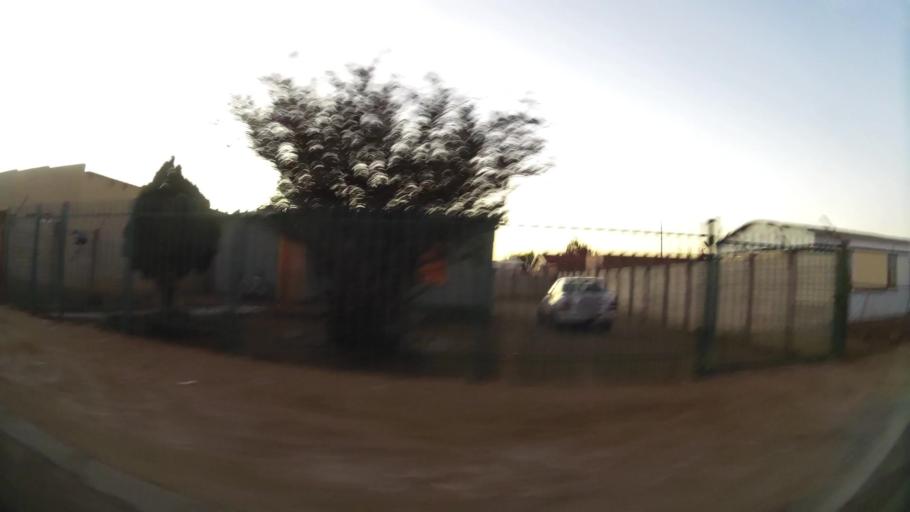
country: ZA
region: Northern Cape
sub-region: Frances Baard District Municipality
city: Kimberley
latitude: -28.7139
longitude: 24.7643
